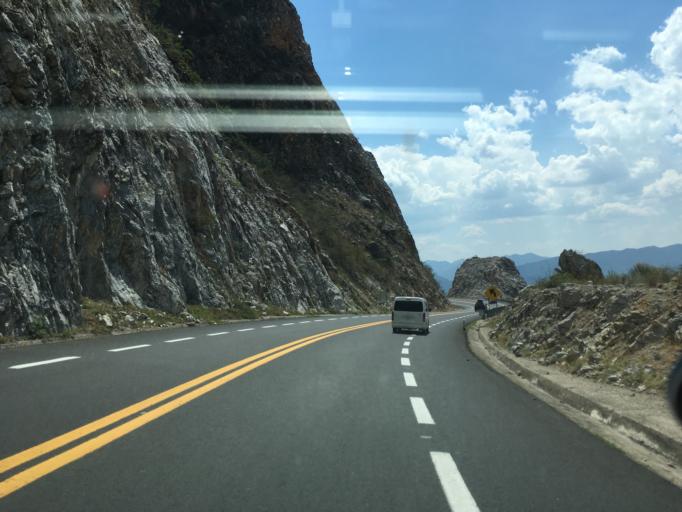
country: MX
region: Puebla
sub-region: San Jose Miahuatlan
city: San Pedro Tetitlan
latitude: 18.0904
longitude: -97.3409
